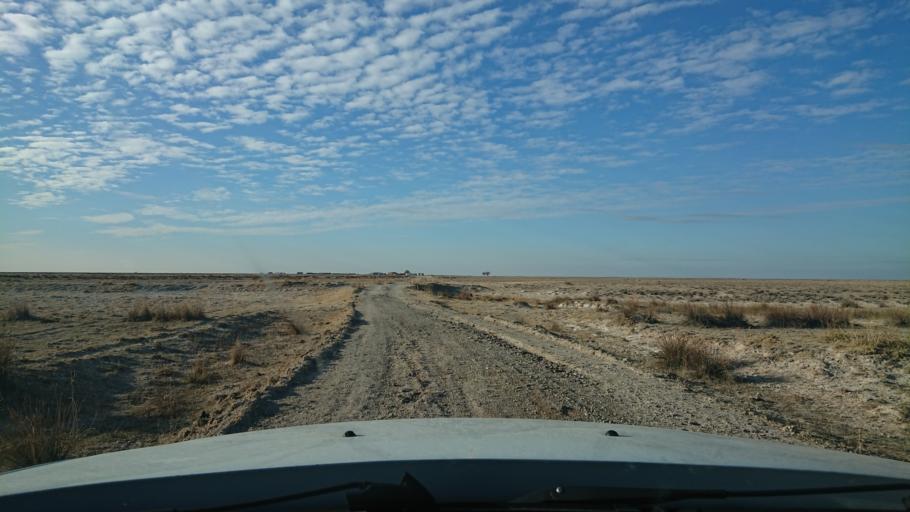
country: TR
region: Aksaray
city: Eskil
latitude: 38.5627
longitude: 33.3061
